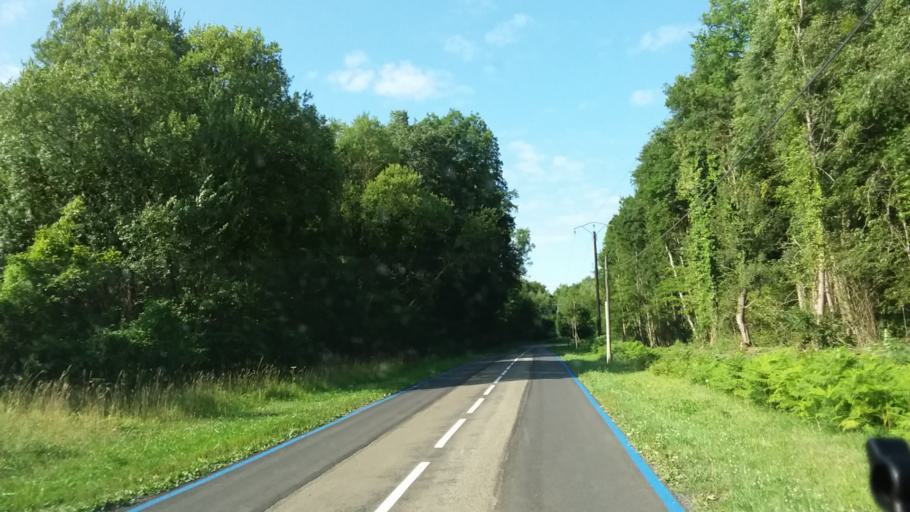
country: FR
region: Picardie
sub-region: Departement de l'Aisne
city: Saint-Erme-Outre-et-Ramecourt
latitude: 49.4535
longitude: 3.8095
